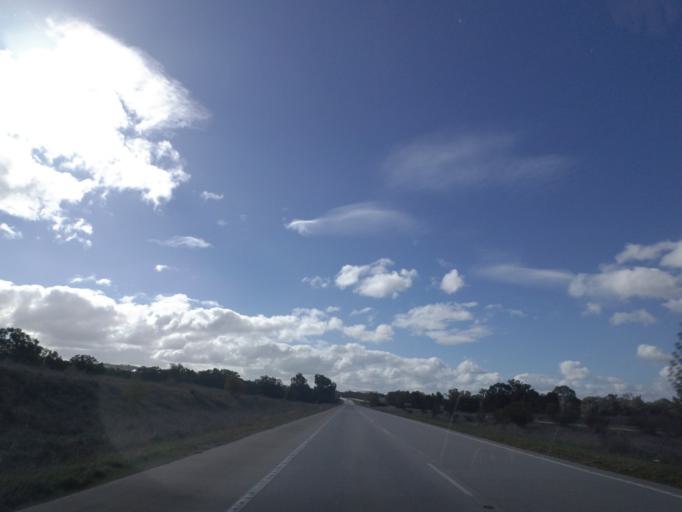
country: AU
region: New South Wales
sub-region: Albury Municipality
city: Lavington
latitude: -36.0082
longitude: 146.9890
